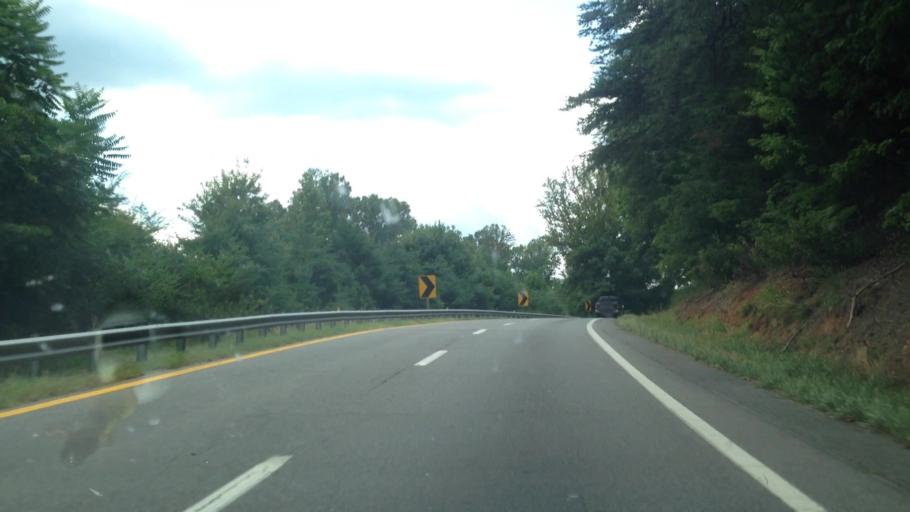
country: US
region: North Carolina
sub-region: Rockingham County
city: Stoneville
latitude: 36.5478
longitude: -79.8994
